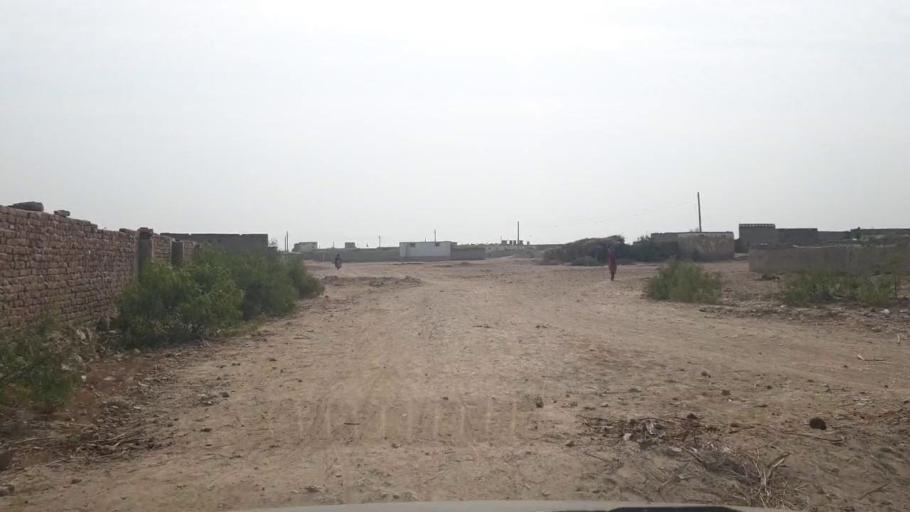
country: PK
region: Sindh
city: Tando Muhammad Khan
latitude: 25.1587
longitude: 68.4708
